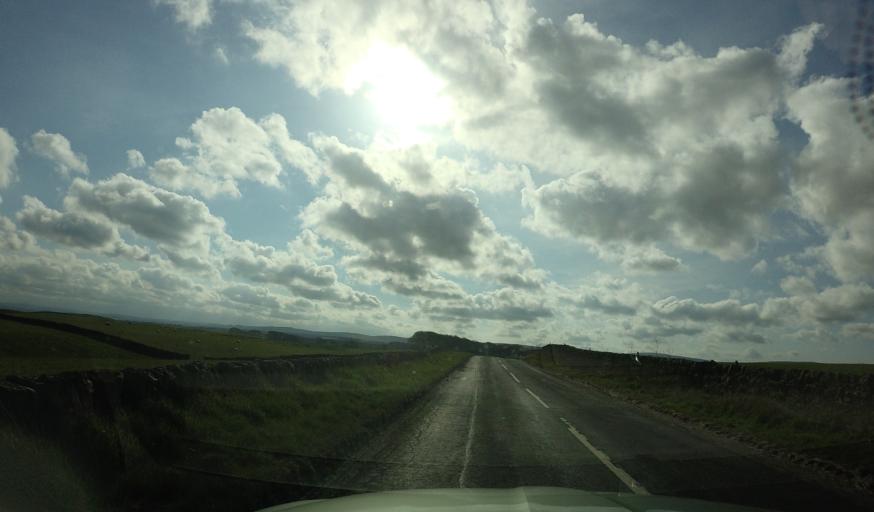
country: GB
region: Scotland
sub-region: Midlothian
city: Penicuik
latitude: 55.8060
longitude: -3.1777
